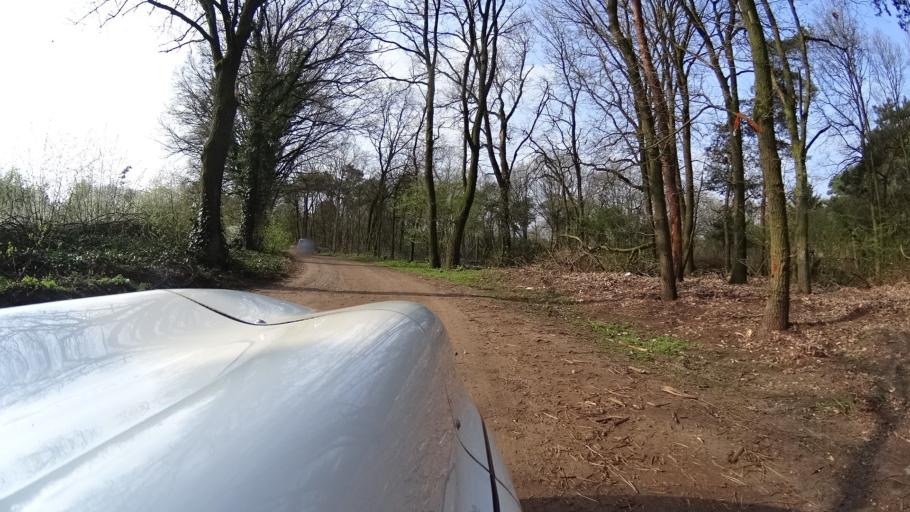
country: NL
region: North Brabant
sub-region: Gemeente Boekel
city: Boekel
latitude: 51.5843
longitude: 5.7045
